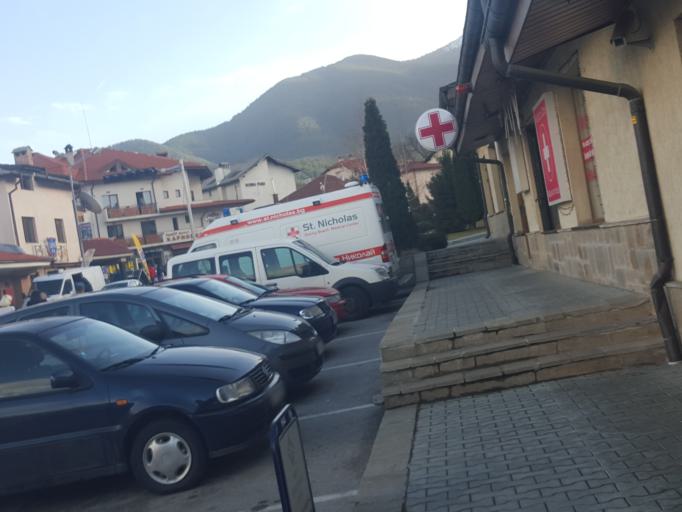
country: BG
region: Blagoevgrad
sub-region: Obshtina Bansko
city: Bansko
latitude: 41.8310
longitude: 23.4805
